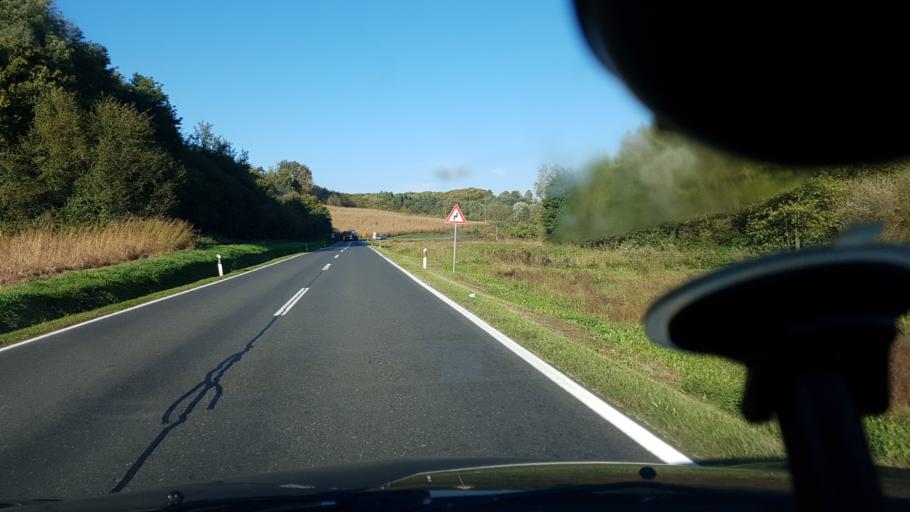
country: HR
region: Koprivnicko-Krizevacka
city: Virje
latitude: 46.0082
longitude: 16.9270
